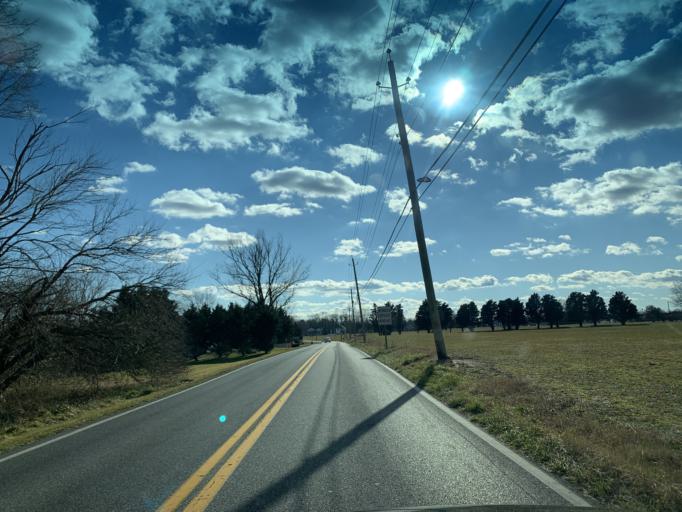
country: US
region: Maryland
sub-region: Worcester County
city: Berlin
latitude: 38.3383
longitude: -75.2202
